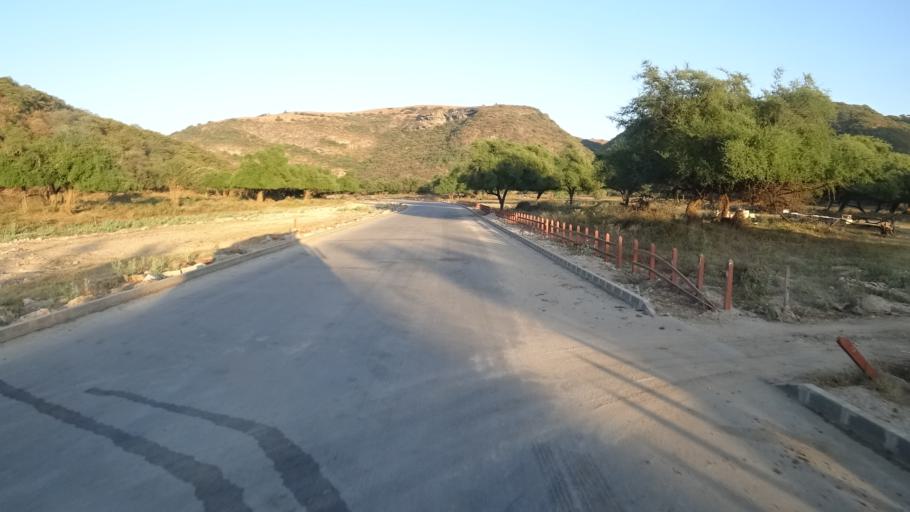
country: OM
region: Zufar
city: Salalah
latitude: 17.0906
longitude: 54.4416
